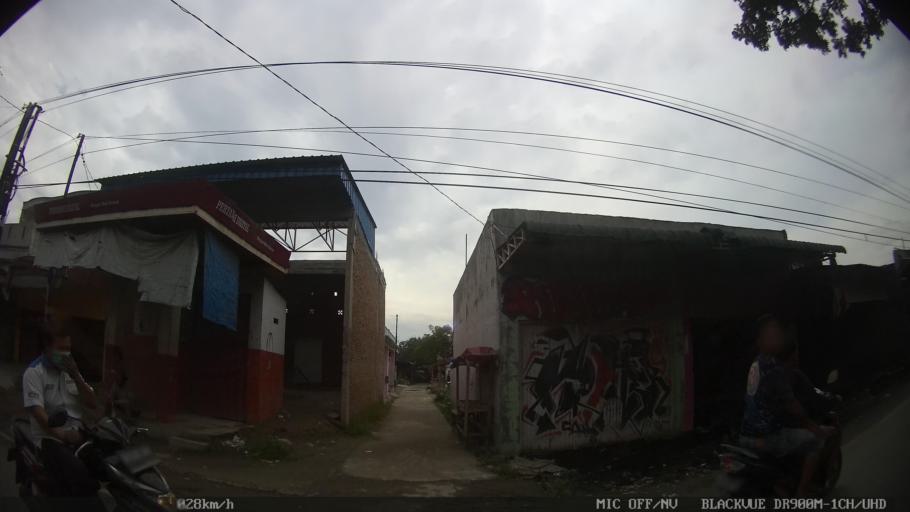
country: ID
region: North Sumatra
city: Sunggal
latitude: 3.6171
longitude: 98.6055
